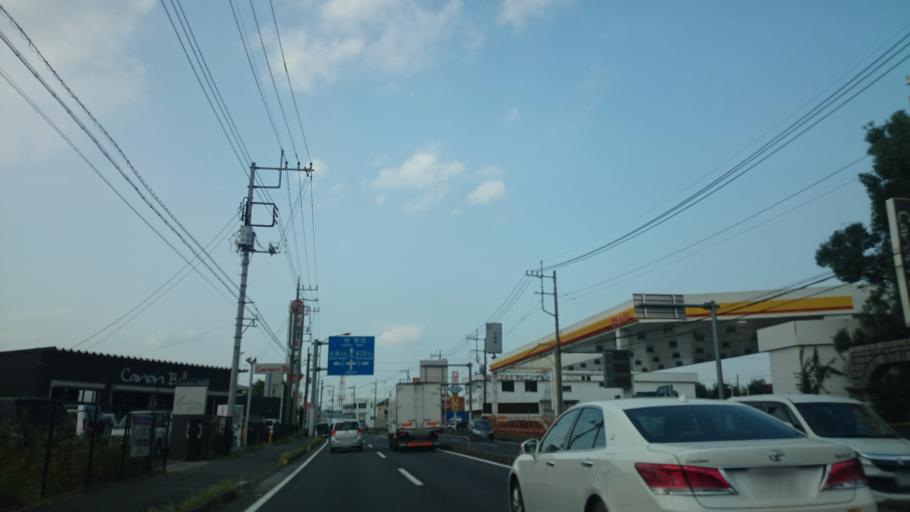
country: JP
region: Saitama
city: Kasukabe
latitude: 35.9692
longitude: 139.7357
